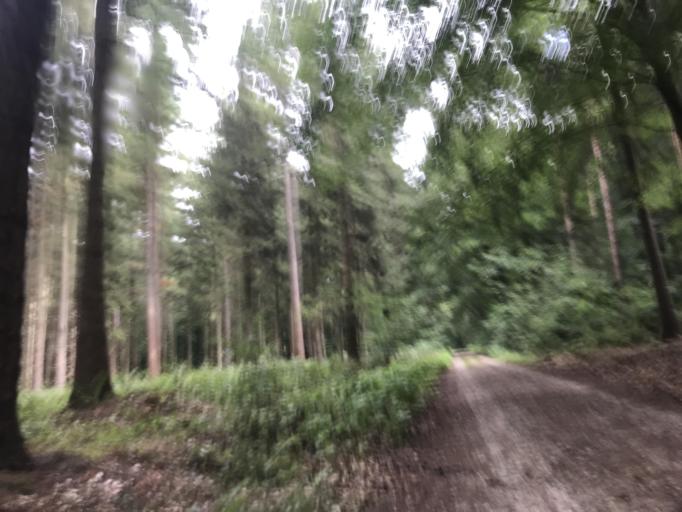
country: DE
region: Lower Saxony
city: Vastorf
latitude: 53.2166
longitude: 10.5445
